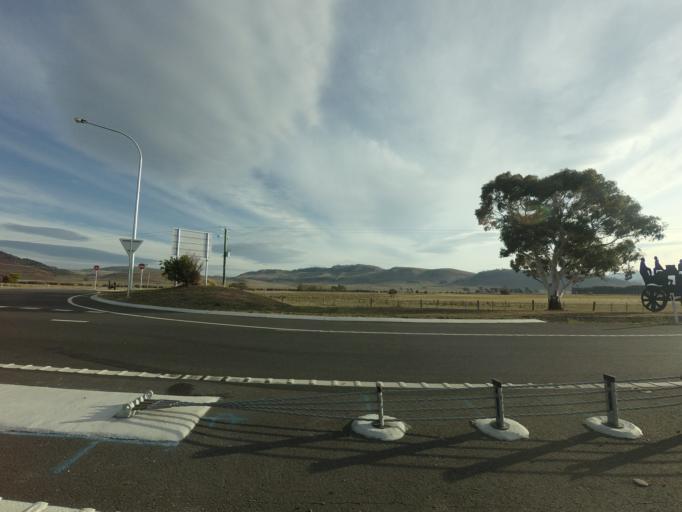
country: AU
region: Tasmania
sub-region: Brighton
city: Bridgewater
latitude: -42.5196
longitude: 147.1921
